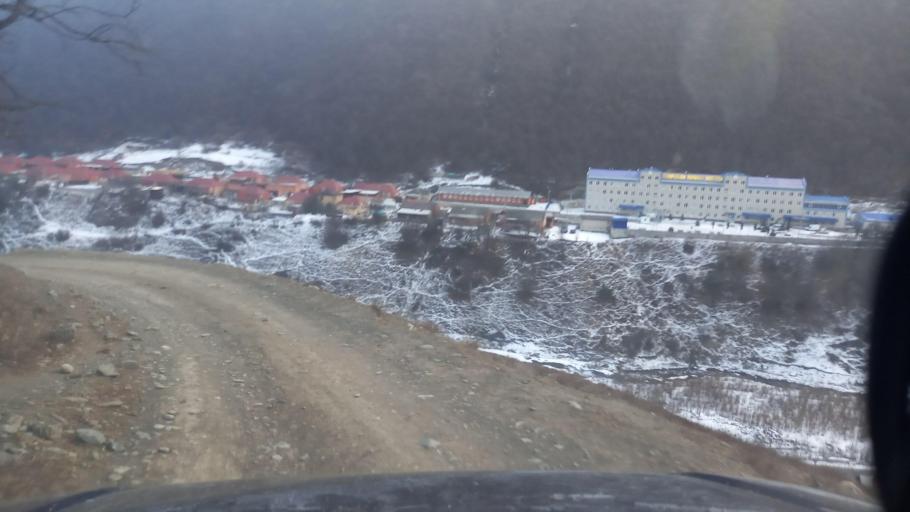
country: RU
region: Ingushetiya
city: Dzhayrakh
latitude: 42.8040
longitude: 44.7533
